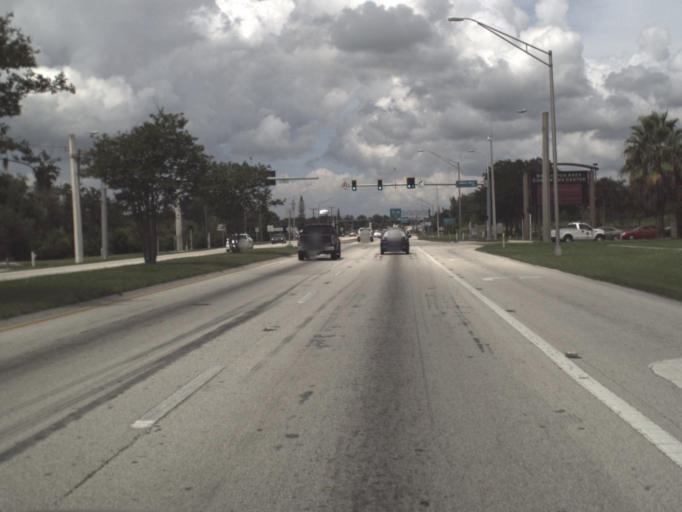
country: US
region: Florida
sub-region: Manatee County
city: Palmetto
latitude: 27.5133
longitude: -82.5630
